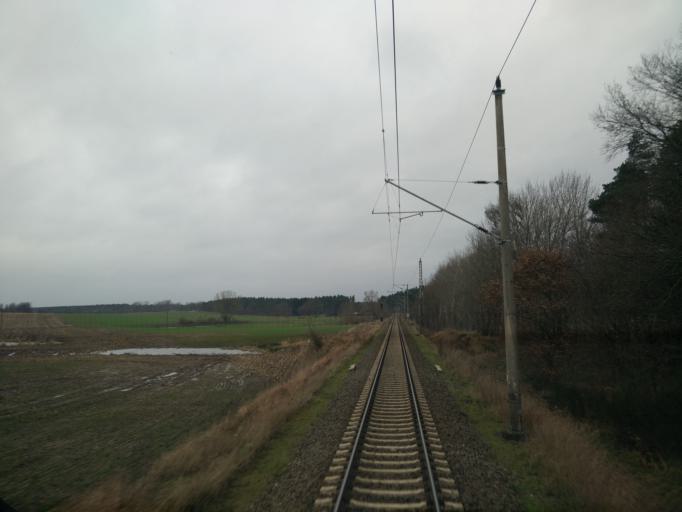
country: DE
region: Mecklenburg-Vorpommern
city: Bad Kleinen
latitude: 53.7820
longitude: 11.4869
